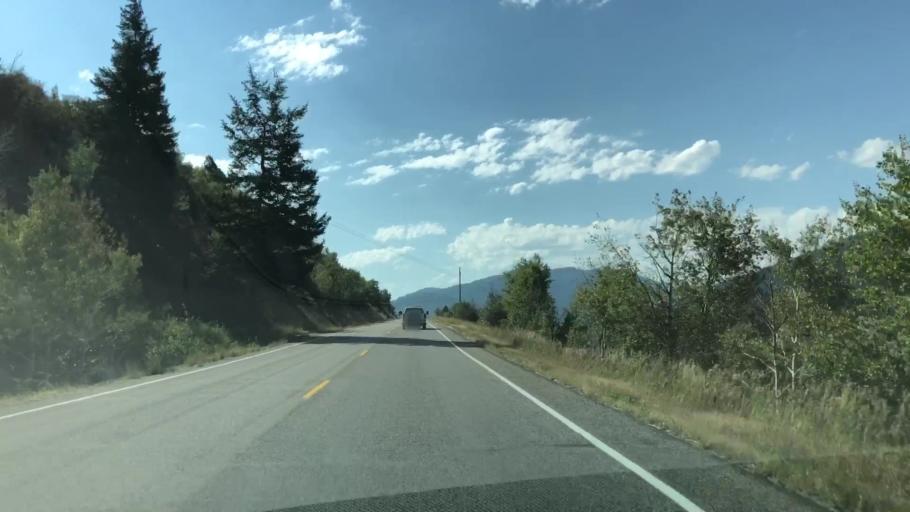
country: US
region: Idaho
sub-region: Teton County
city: Victor
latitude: 43.3385
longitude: -111.2002
